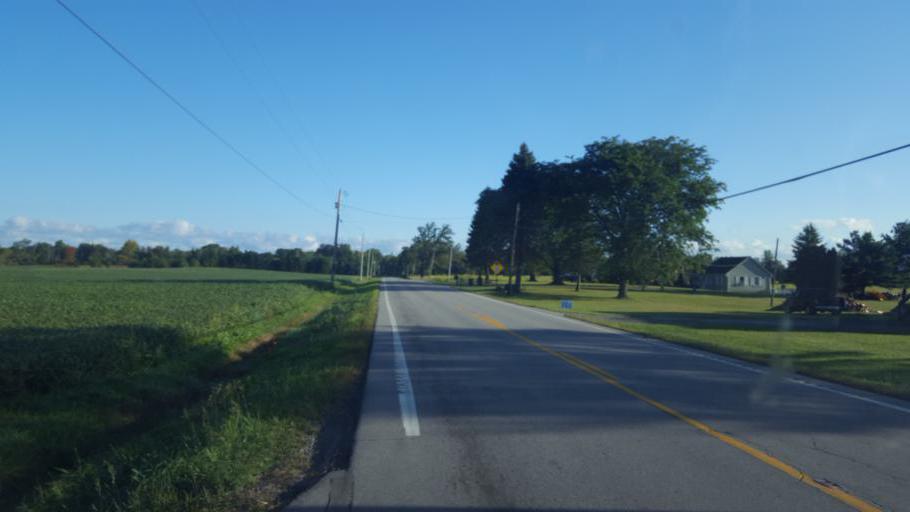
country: US
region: Ohio
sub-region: Lorain County
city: Wellington
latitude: 41.1156
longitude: -82.3036
